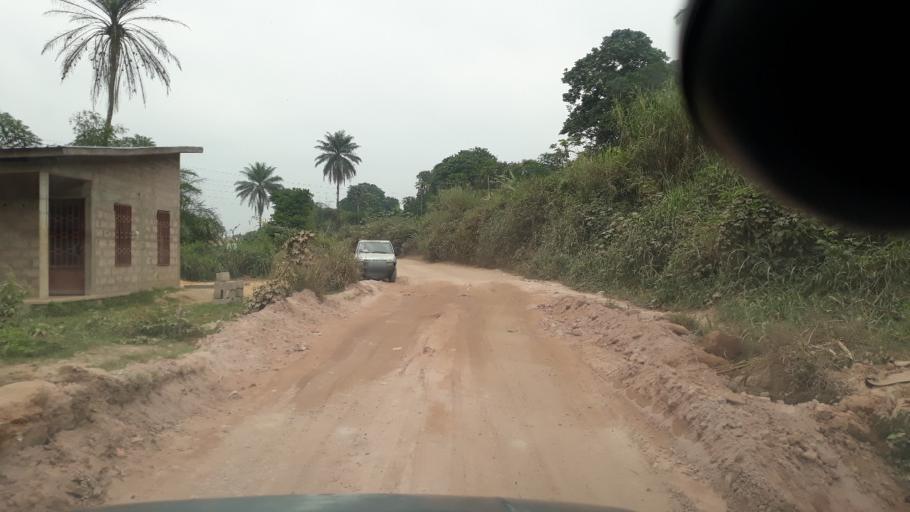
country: CD
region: Kinshasa
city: Masina
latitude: -4.4756
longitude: 15.2768
